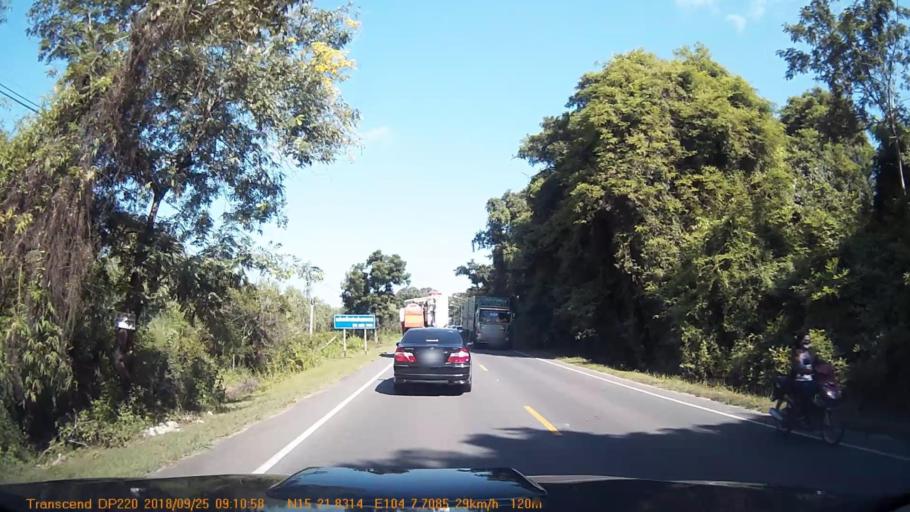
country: TH
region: Sisaket
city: Rasi Salai
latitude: 15.3638
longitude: 104.1285
